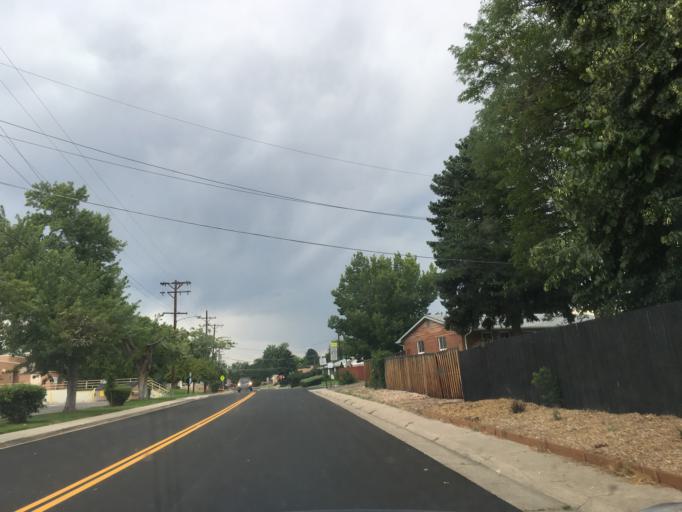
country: US
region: Colorado
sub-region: Arapahoe County
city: Sheridan
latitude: 39.6733
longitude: -105.0431
